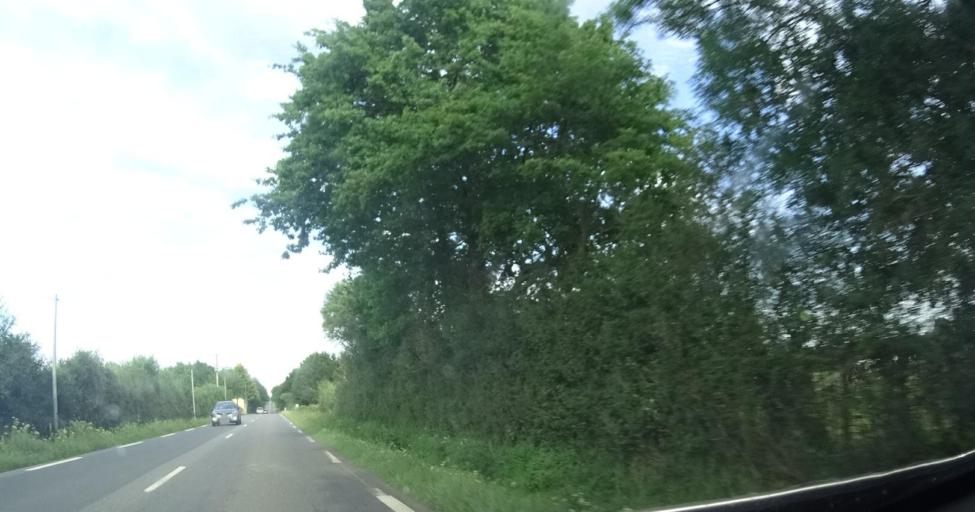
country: FR
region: Pays de la Loire
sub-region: Departement de la Loire-Atlantique
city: Notre-Dame-des-Landes
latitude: 47.4101
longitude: -1.7076
